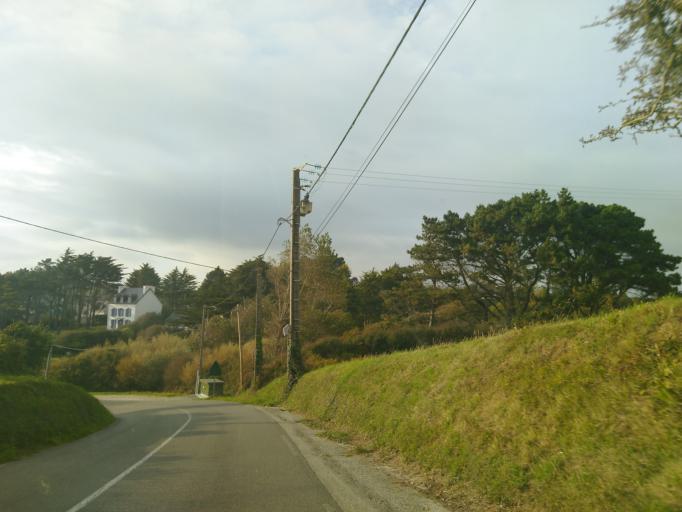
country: FR
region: Brittany
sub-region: Departement du Finistere
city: Crozon
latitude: 48.2385
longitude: -4.4615
